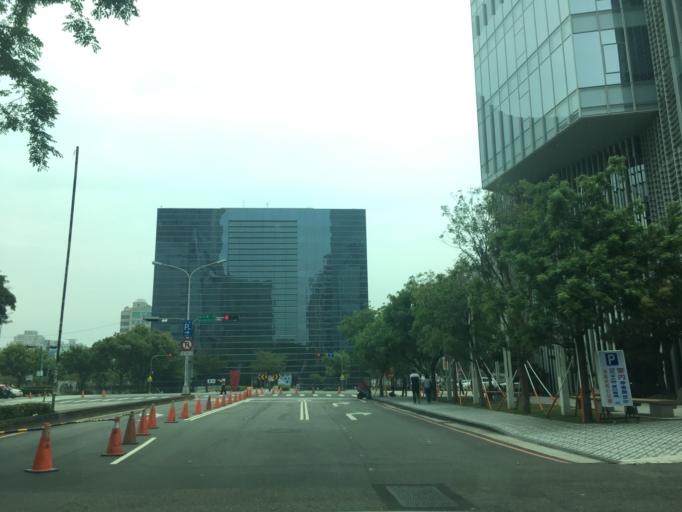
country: TW
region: Taiwan
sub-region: Taichung City
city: Taichung
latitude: 24.1629
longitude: 120.6446
